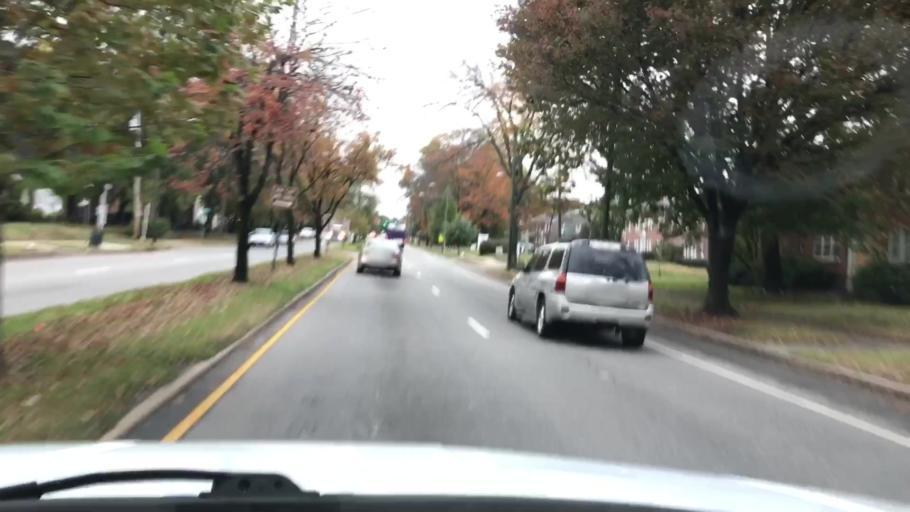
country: US
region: Virginia
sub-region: Henrico County
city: Lakeside
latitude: 37.5991
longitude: -77.4498
